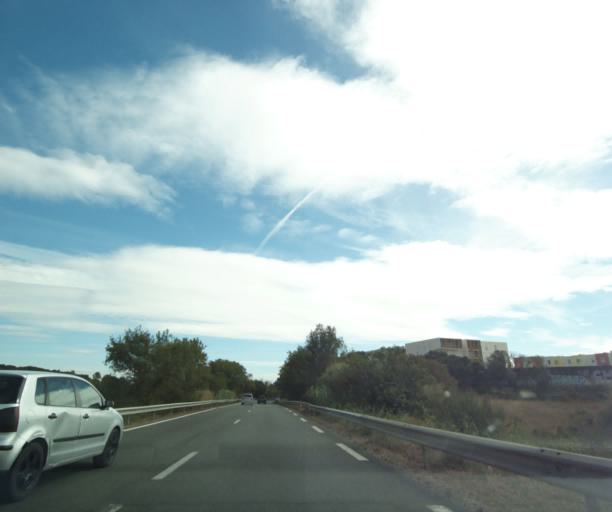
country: FR
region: Languedoc-Roussillon
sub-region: Departement de l'Herault
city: Juvignac
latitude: 43.6237
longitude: 3.7878
